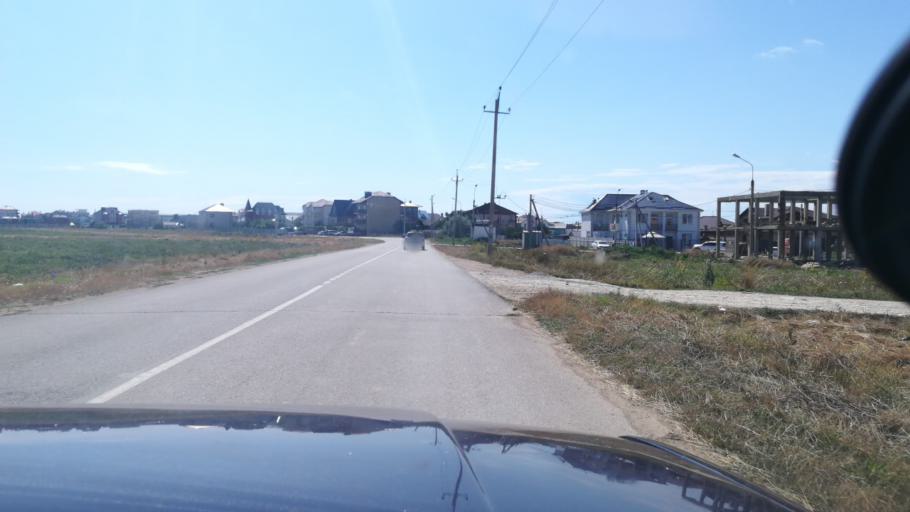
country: RU
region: Krasnodarskiy
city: Vityazevo
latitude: 44.9882
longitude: 37.2741
